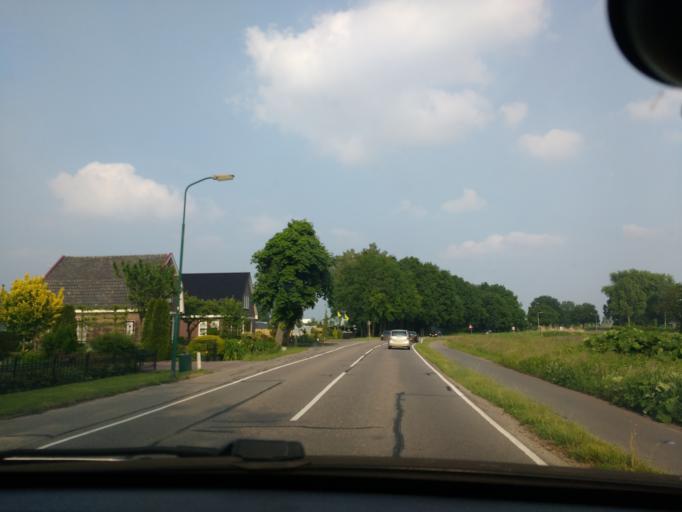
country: NL
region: Utrecht
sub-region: Gemeente Veenendaal
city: Veenendaal
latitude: 52.0343
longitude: 5.5872
